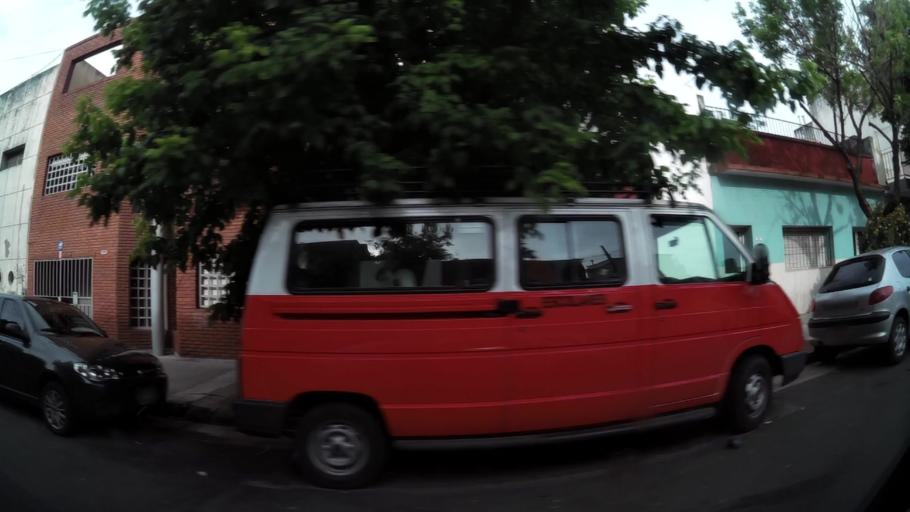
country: AR
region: Buenos Aires F.D.
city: Buenos Aires
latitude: -34.6336
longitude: -58.4267
